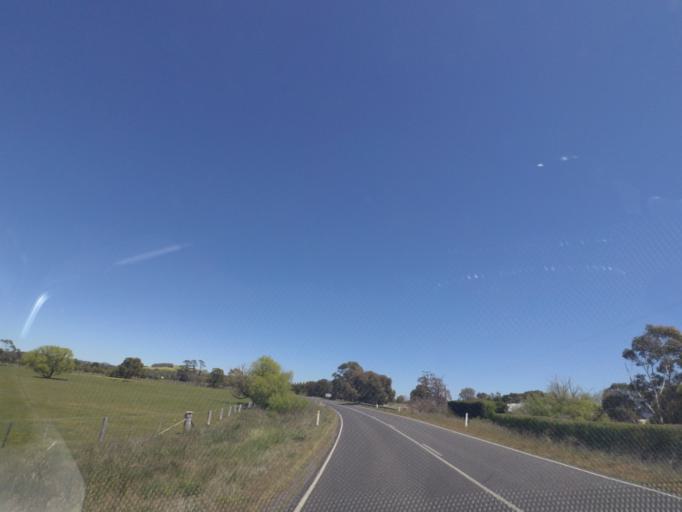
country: AU
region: Victoria
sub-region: Hume
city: Sunbury
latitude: -37.2793
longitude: 144.7151
